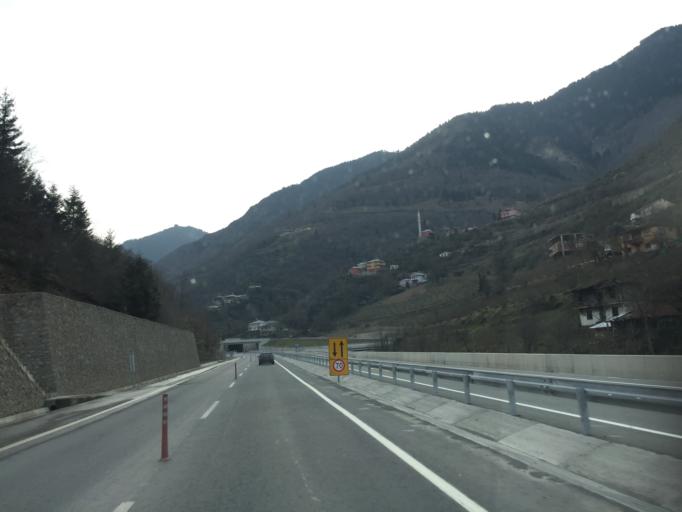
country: TR
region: Trabzon
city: Macka
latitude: 40.7819
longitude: 39.5724
